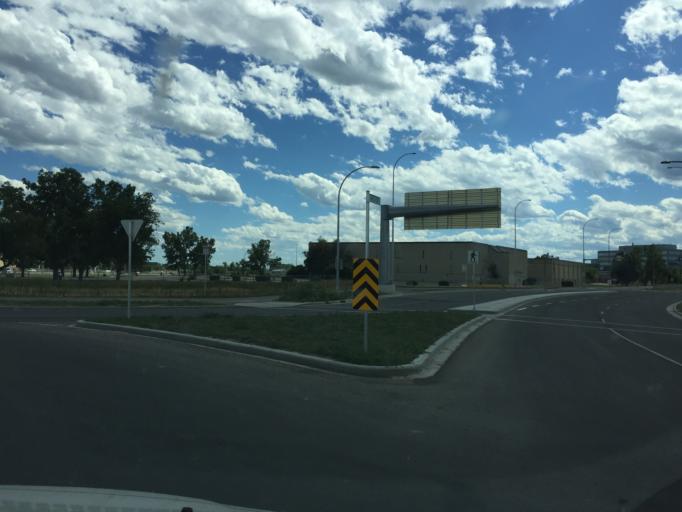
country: CA
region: Alberta
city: Calgary
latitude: 51.0150
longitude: -114.1195
